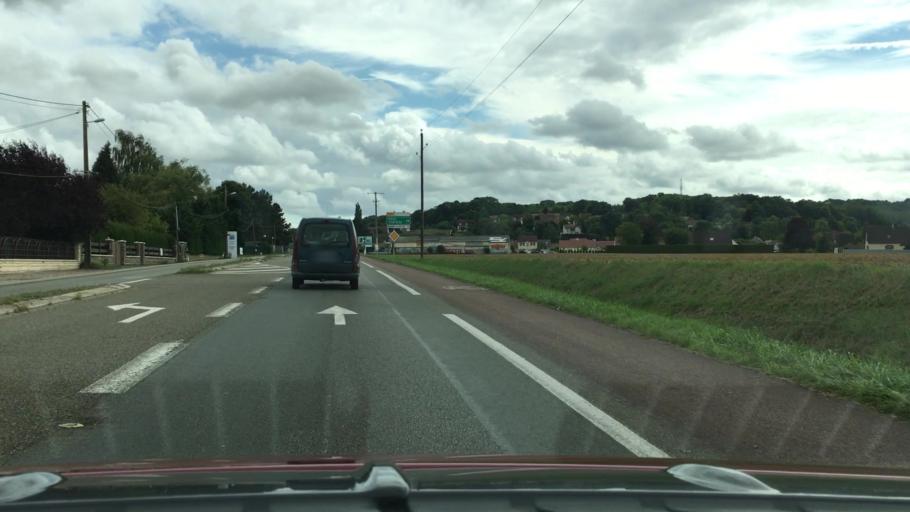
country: FR
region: Haute-Normandie
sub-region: Departement de l'Eure
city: Gisors
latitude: 49.2650
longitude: 1.7845
